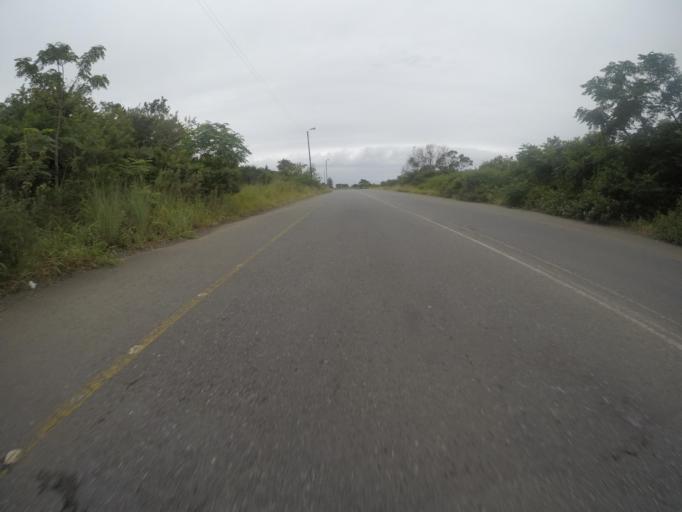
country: ZA
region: Eastern Cape
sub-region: Buffalo City Metropolitan Municipality
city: East London
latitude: -32.9691
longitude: 27.8628
